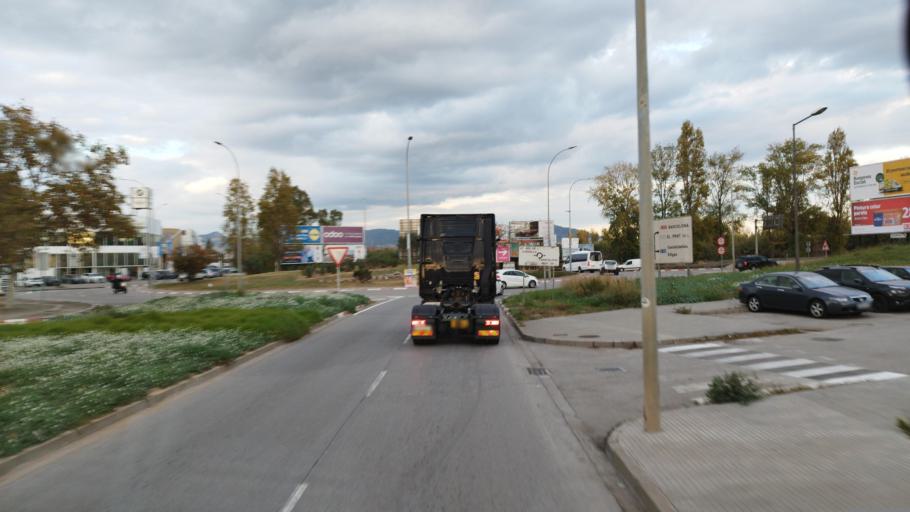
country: ES
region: Catalonia
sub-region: Provincia de Barcelona
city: Sant Boi de Llobregat
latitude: 41.3339
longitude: 2.0518
